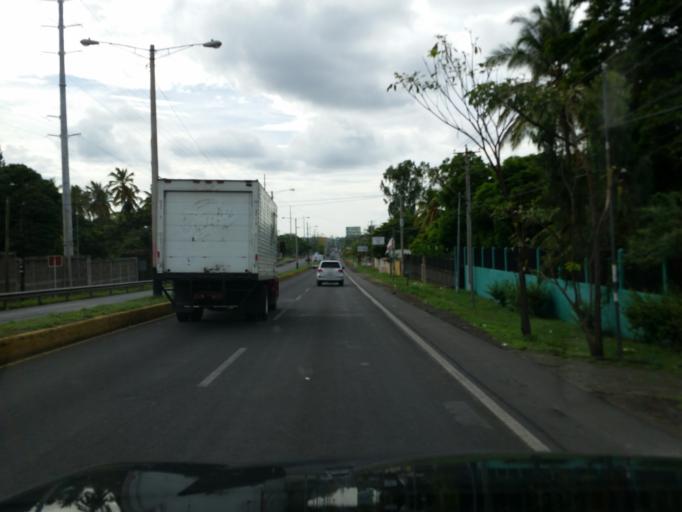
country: NI
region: Masaya
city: Ticuantepe
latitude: 12.0505
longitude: -86.1982
